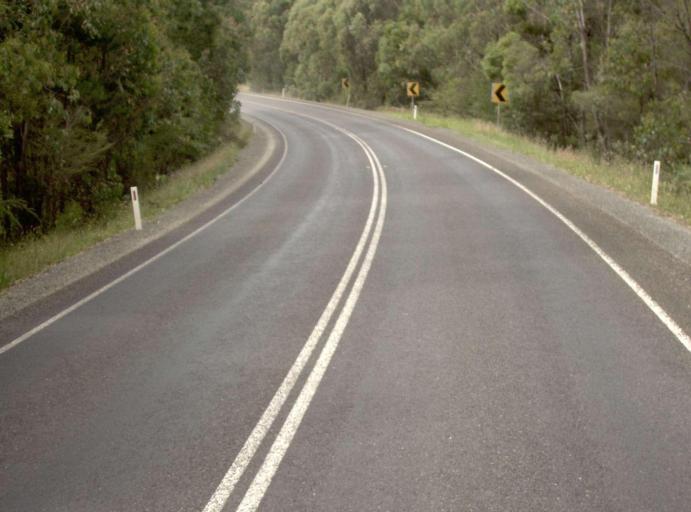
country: AU
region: Victoria
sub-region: Latrobe
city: Traralgon
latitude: -38.1161
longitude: 146.4514
